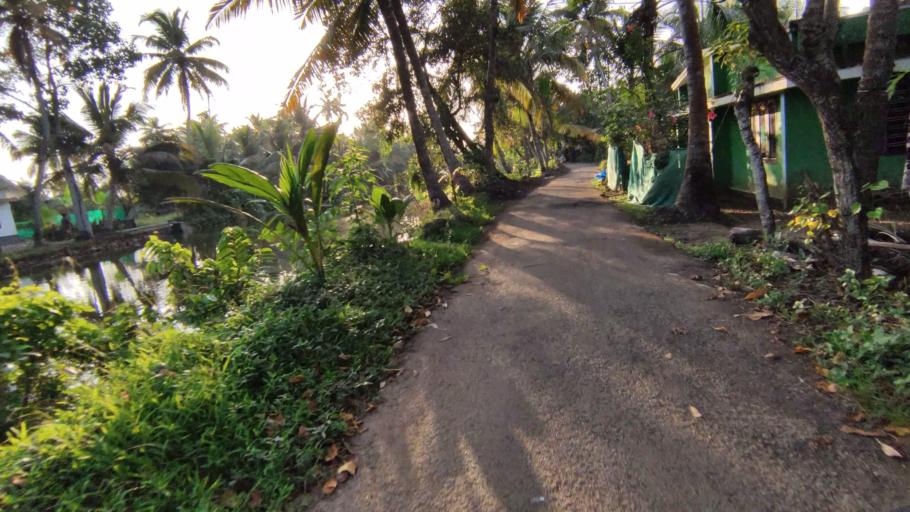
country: IN
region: Kerala
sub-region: Kottayam
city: Kottayam
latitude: 9.5762
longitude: 76.4484
